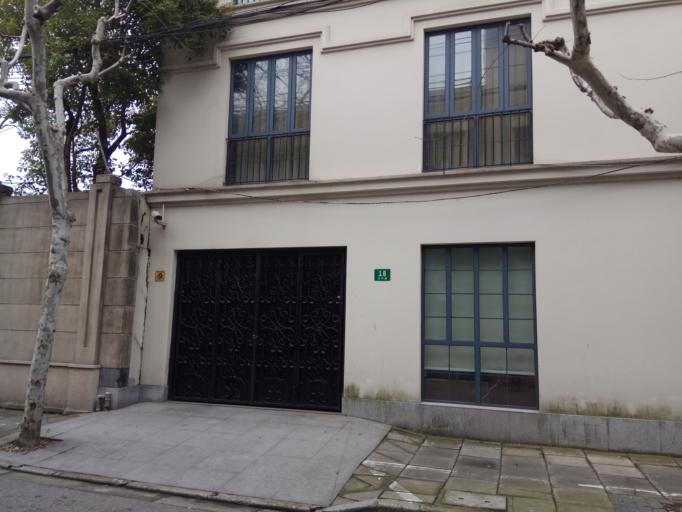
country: CN
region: Shanghai Shi
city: Xuhui
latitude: 31.2106
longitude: 121.4440
